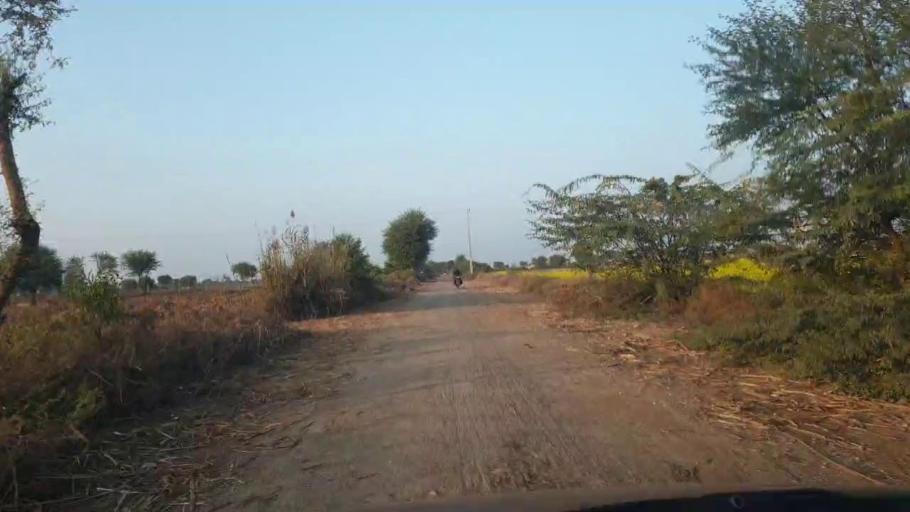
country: PK
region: Sindh
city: Berani
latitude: 25.8452
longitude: 68.7448
